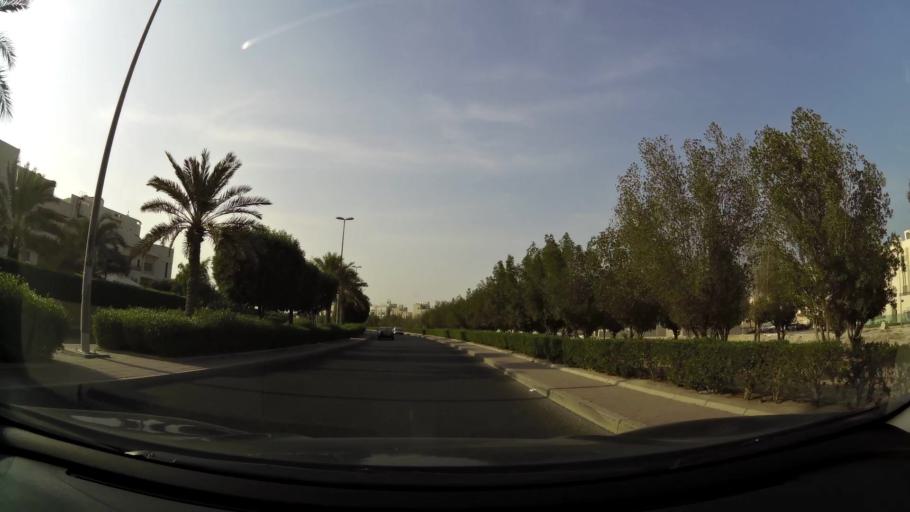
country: KW
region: Mubarak al Kabir
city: Mubarak al Kabir
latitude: 29.1936
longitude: 48.0972
